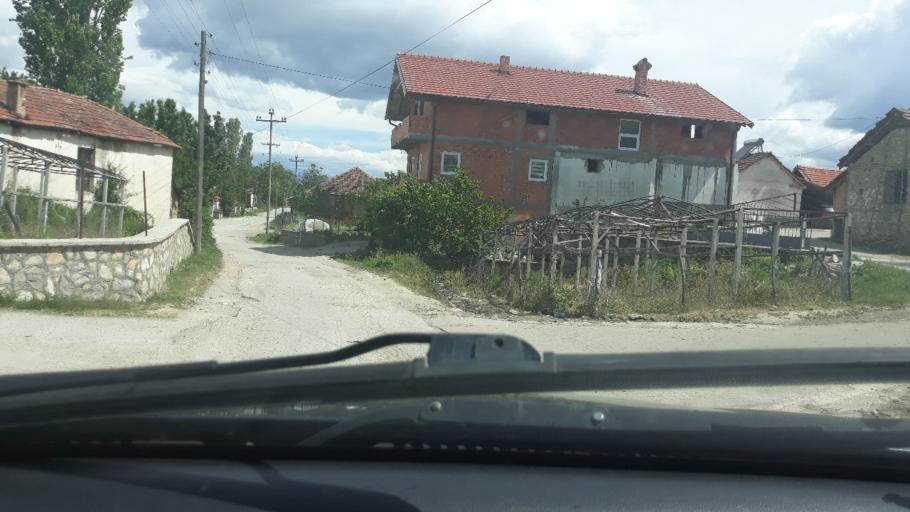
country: MK
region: Krivogastani
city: Krivogashtani
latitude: 41.3215
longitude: 21.3053
